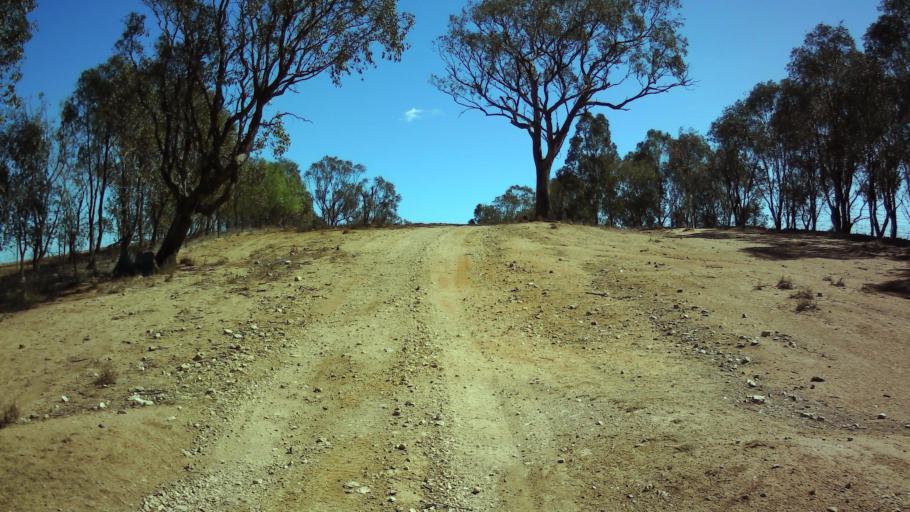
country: AU
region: New South Wales
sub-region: Weddin
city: Grenfell
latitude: -33.9960
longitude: 148.4361
